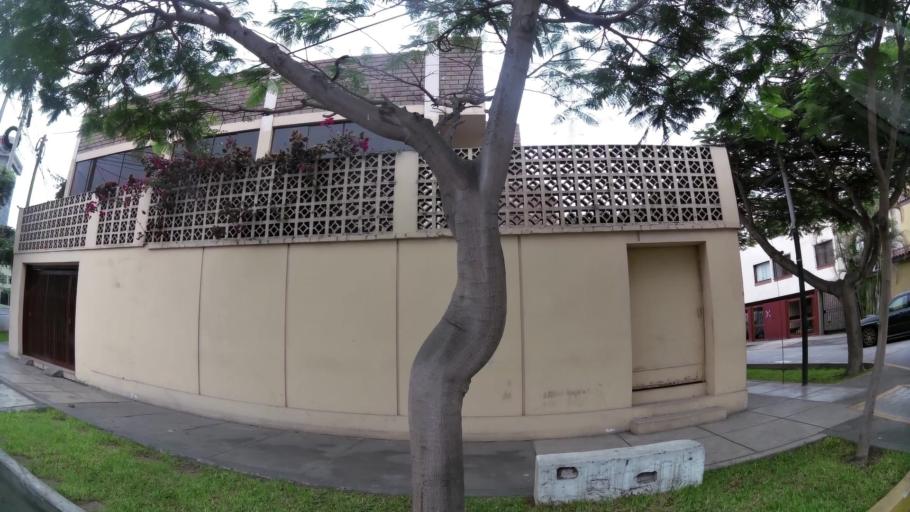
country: PE
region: Lima
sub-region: Lima
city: San Luis
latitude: -12.0989
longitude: -77.0172
